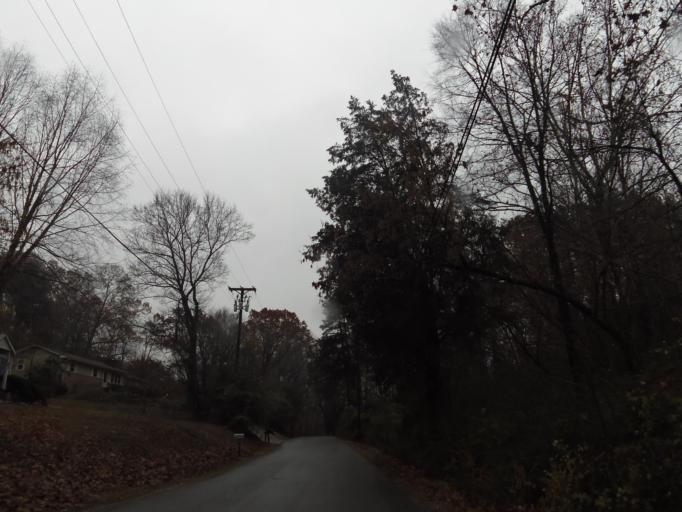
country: US
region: Tennessee
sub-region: Knox County
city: Knoxville
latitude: 35.9128
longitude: -83.9463
